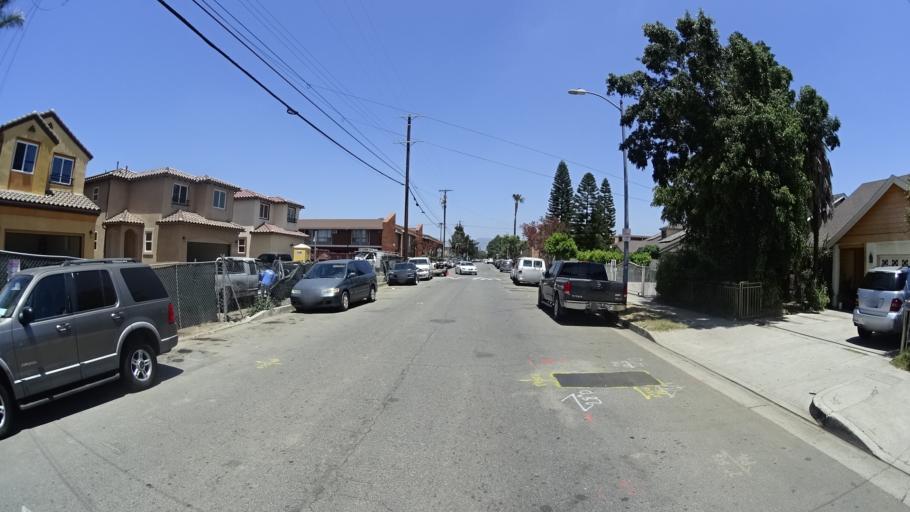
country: US
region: California
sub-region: Los Angeles County
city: Van Nuys
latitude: 34.2268
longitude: -118.4611
